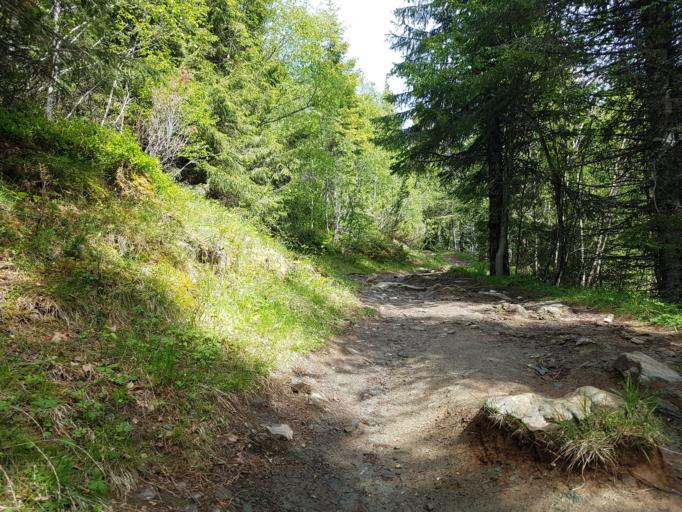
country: NO
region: Sor-Trondelag
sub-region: Trondheim
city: Trondheim
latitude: 63.4268
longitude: 10.3030
